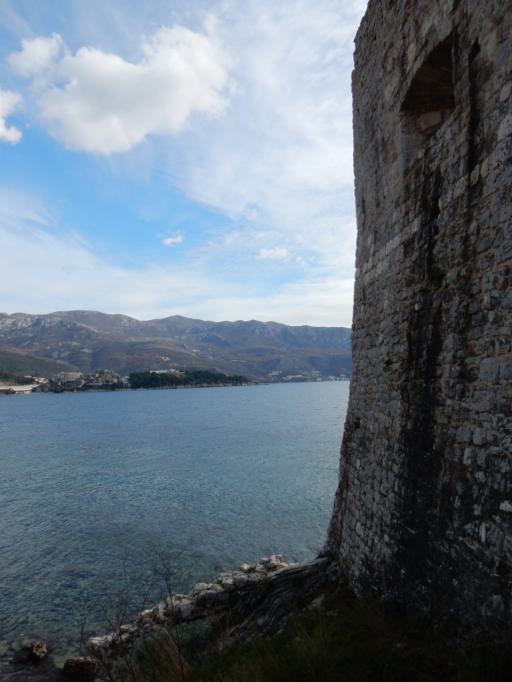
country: ME
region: Budva
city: Budva
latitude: 42.2771
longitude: 18.8386
